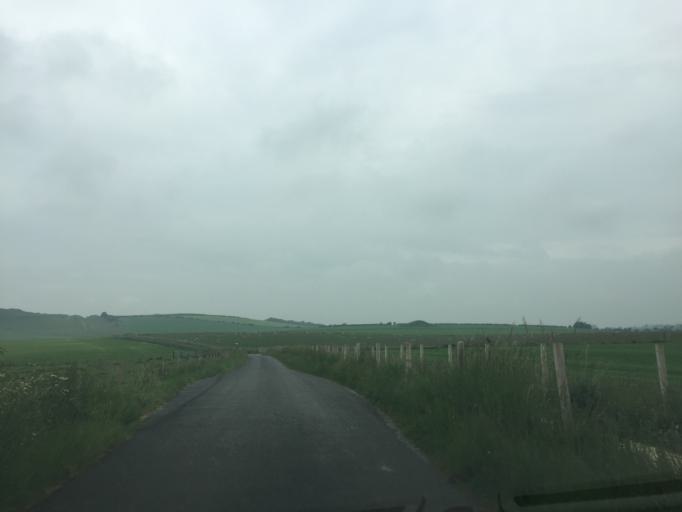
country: GB
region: England
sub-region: Dorset
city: Dorchester
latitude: 50.7025
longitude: -2.4619
